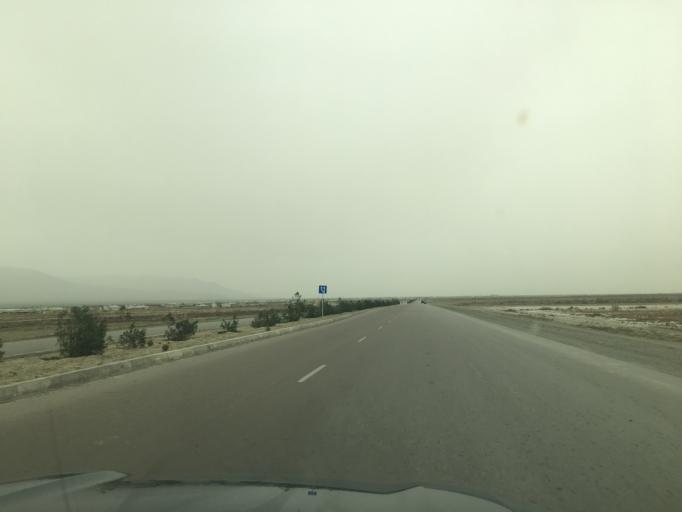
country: TM
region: Ahal
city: Baharly
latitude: 38.3744
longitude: 57.5116
